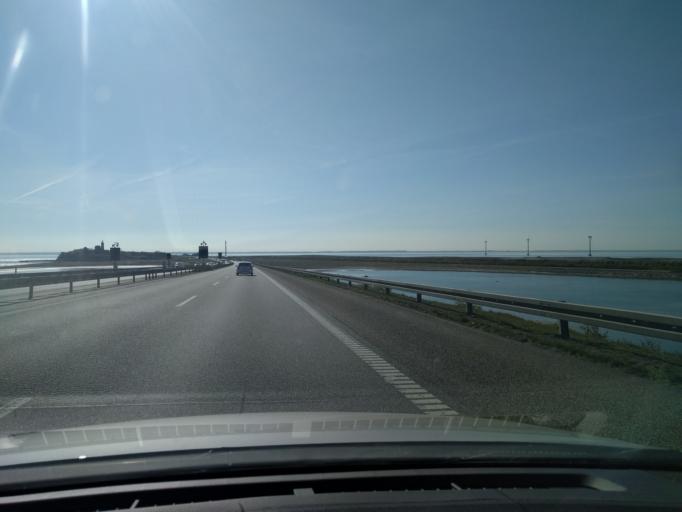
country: DK
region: Zealand
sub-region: Slagelse Kommune
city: Korsor
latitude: 55.3349
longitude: 10.9859
